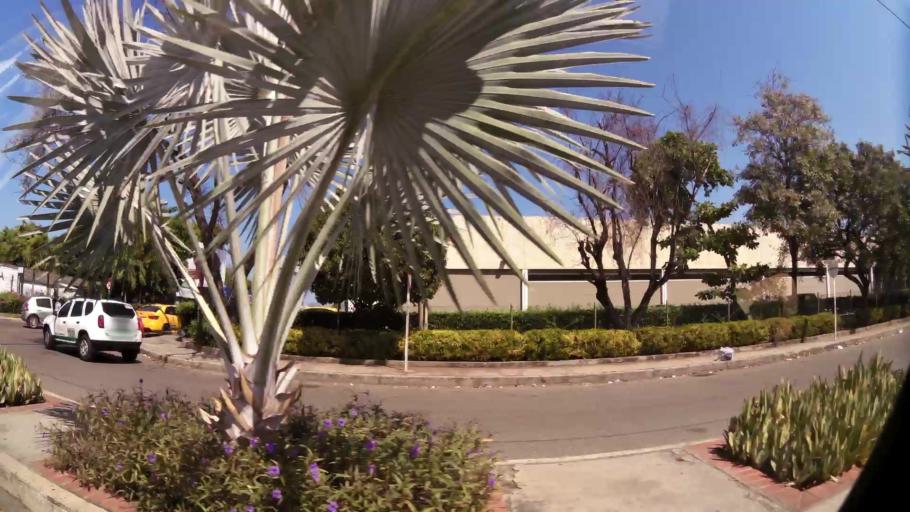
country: CO
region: Bolivar
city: Cartagena
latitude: 10.4444
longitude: -75.5165
